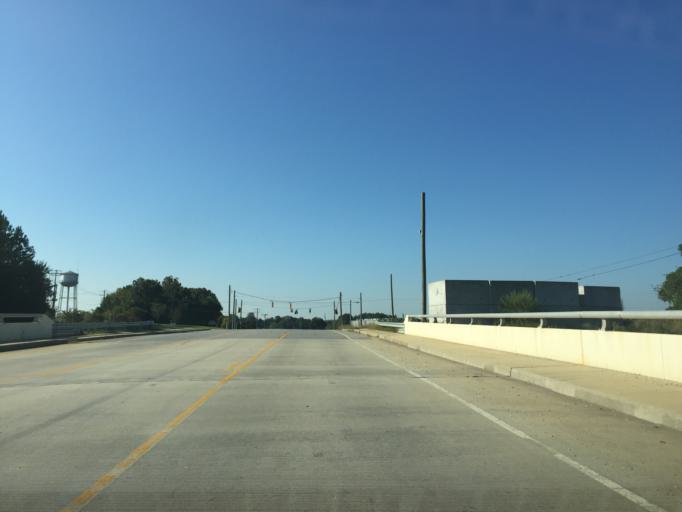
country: US
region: Tennessee
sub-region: Hamilton County
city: Harrison
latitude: 35.0782
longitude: -85.1537
